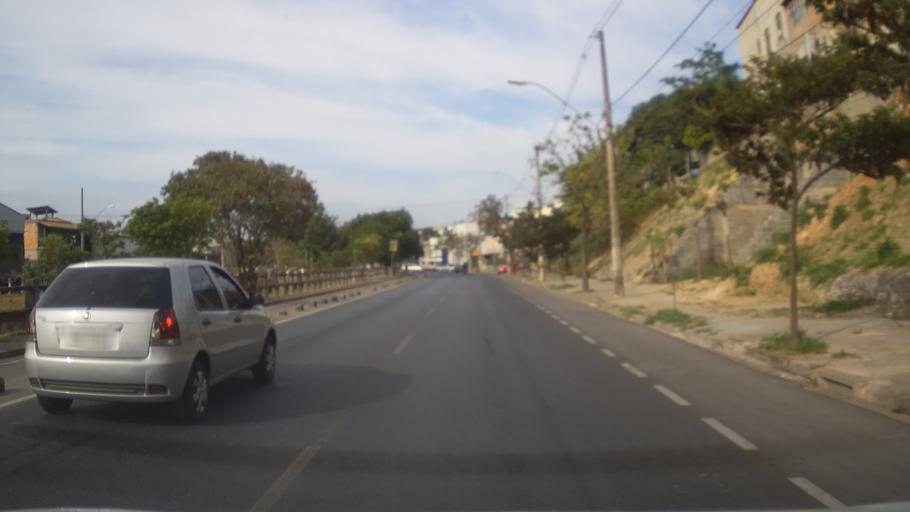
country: BR
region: Minas Gerais
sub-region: Contagem
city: Contagem
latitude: -19.8677
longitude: -44.0103
